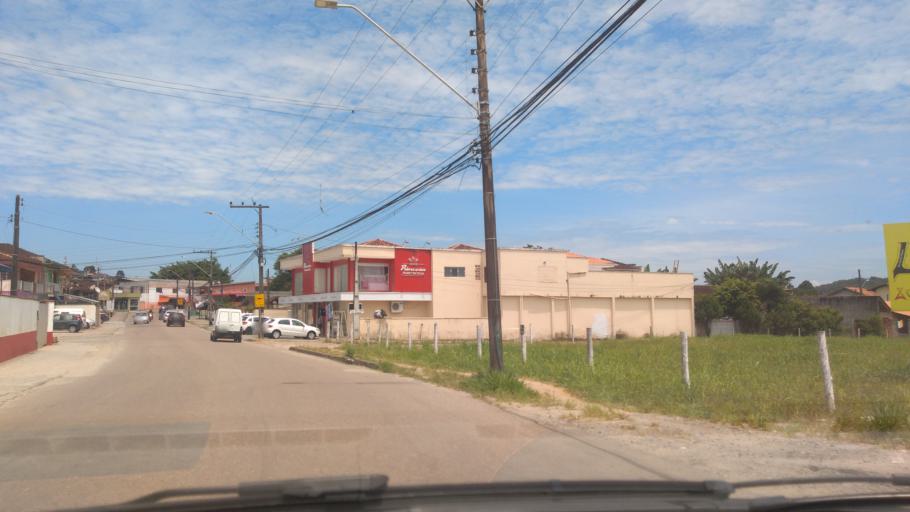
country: BR
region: Santa Catarina
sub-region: Joinville
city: Joinville
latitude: -26.3275
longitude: -48.8098
